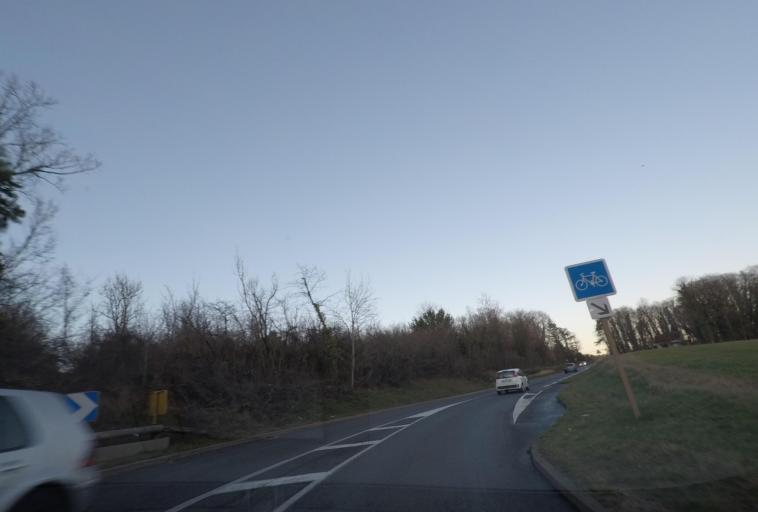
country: FR
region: Ile-de-France
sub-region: Departement de l'Essonne
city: Mennecy
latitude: 48.5794
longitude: 2.4322
